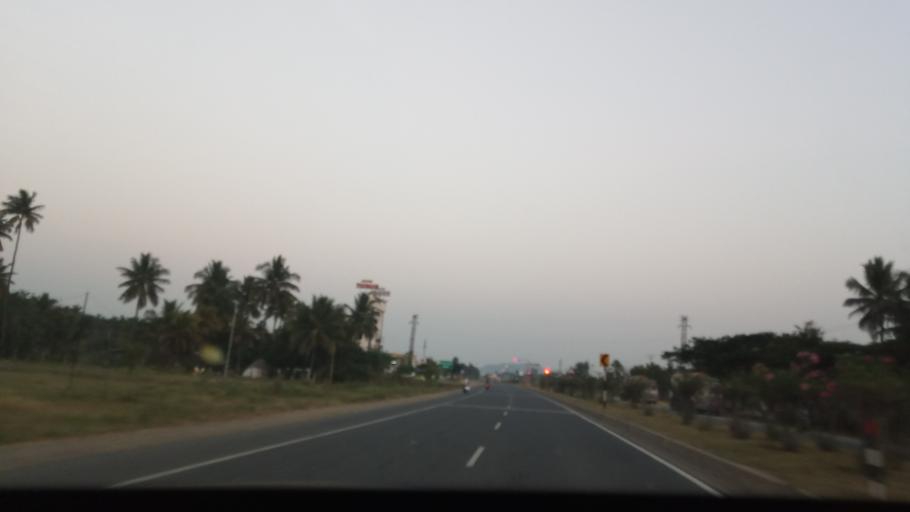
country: IN
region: Tamil Nadu
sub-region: Salem
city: Belur
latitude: 11.6541
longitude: 78.3423
